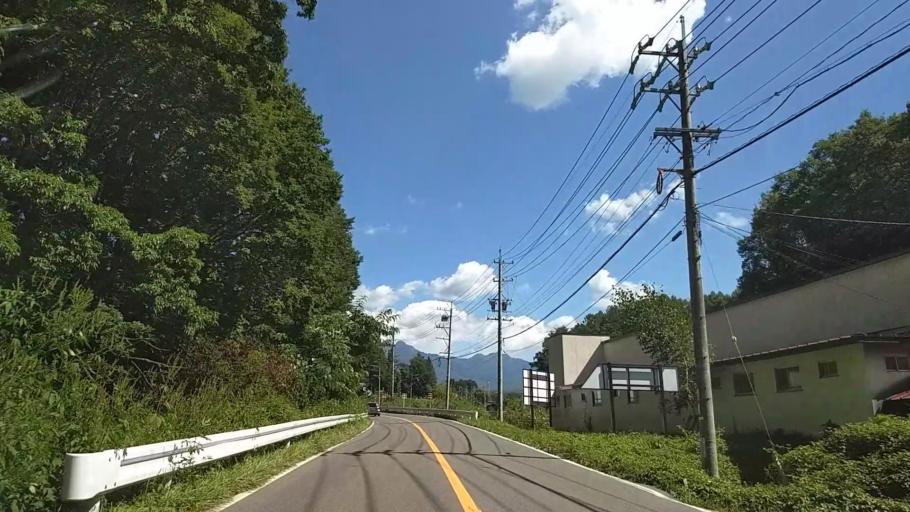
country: JP
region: Nagano
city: Chino
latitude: 36.0316
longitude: 138.2068
